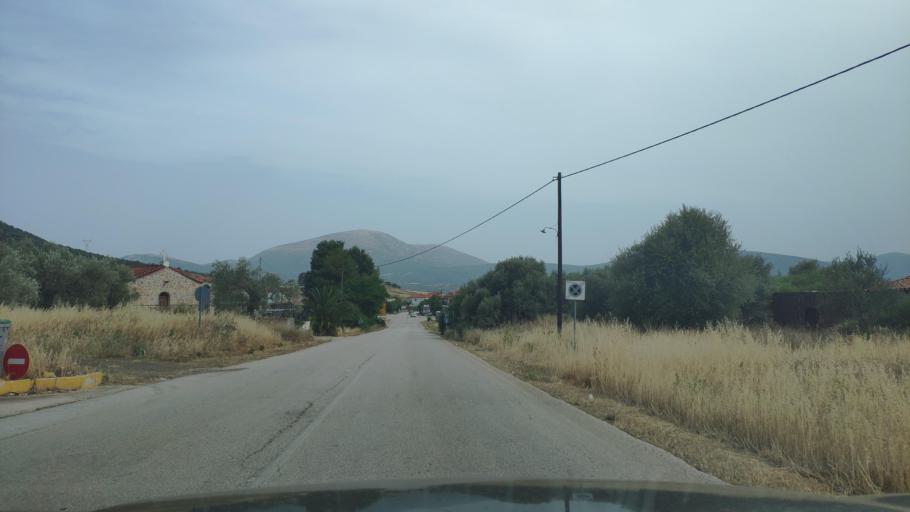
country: GR
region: Peloponnese
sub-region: Nomos Argolidos
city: Palaia Epidavros
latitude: 37.5638
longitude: 23.1512
